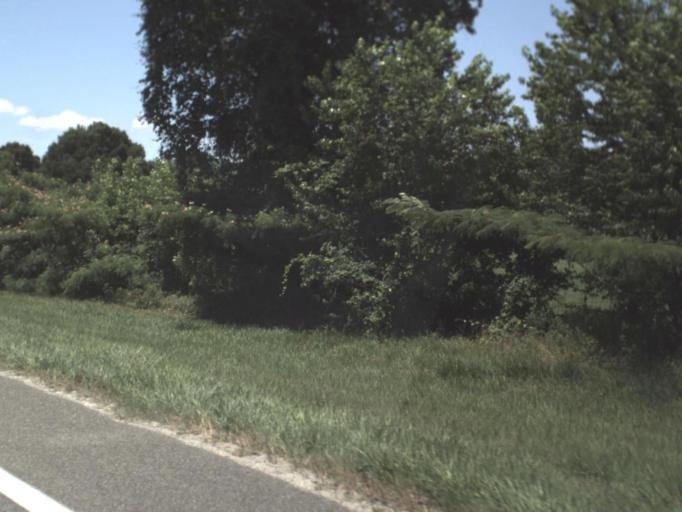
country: US
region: Florida
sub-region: Lafayette County
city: Mayo
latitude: 29.9745
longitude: -82.9865
